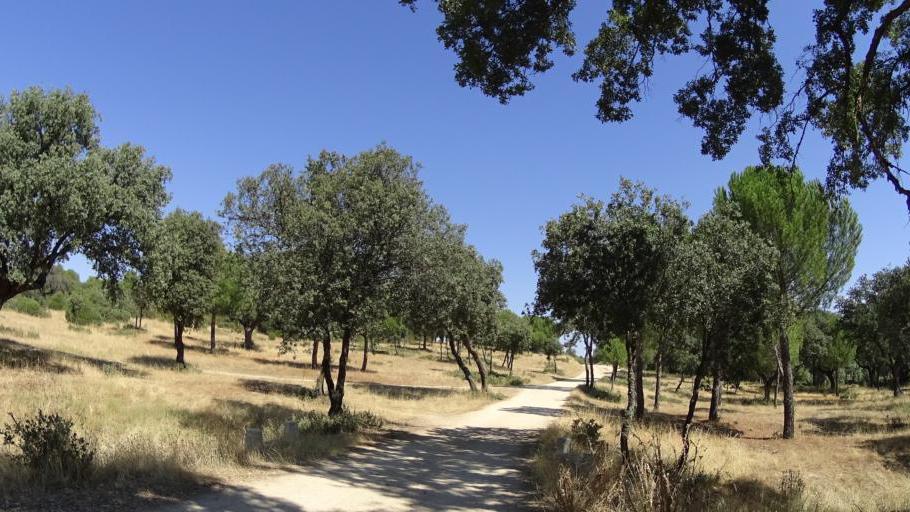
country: ES
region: Madrid
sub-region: Provincia de Madrid
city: Boadilla del Monte
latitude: 40.4260
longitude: -3.8541
